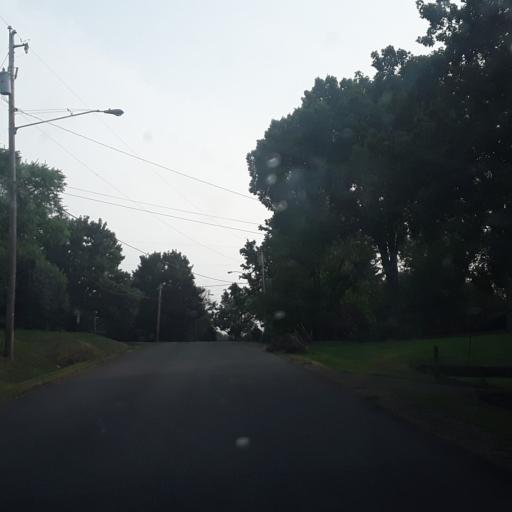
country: US
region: Tennessee
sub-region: Davidson County
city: Oak Hill
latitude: 36.0717
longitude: -86.7493
